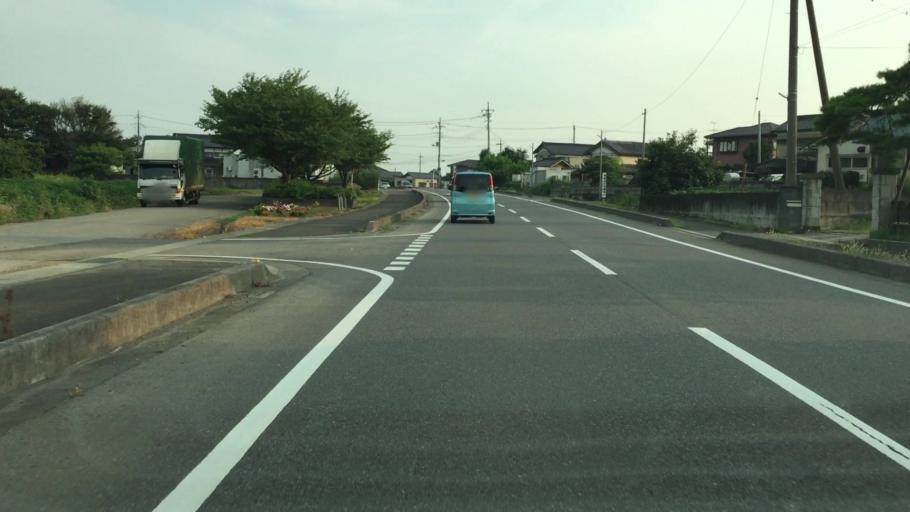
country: JP
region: Gunma
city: Tatebayashi
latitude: 36.2359
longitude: 139.5905
